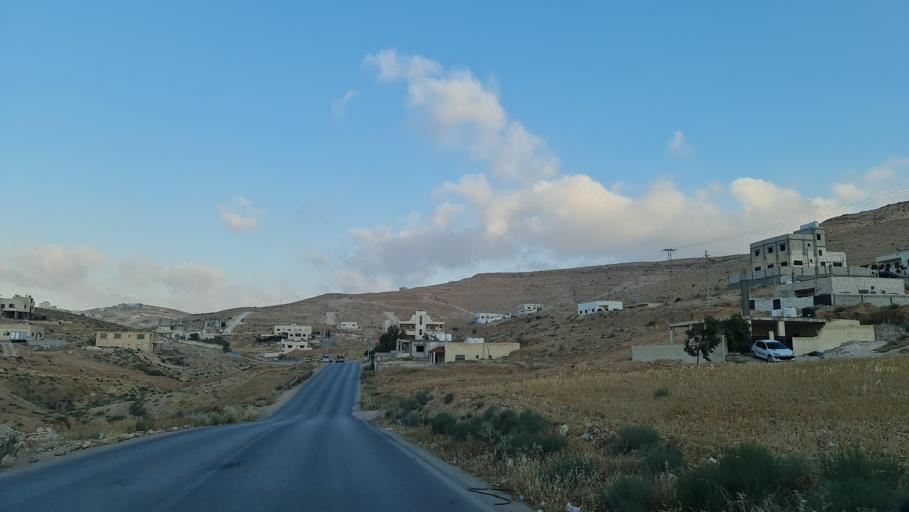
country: JO
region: Zarqa
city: Zarqa
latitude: 32.0829
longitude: 36.0511
